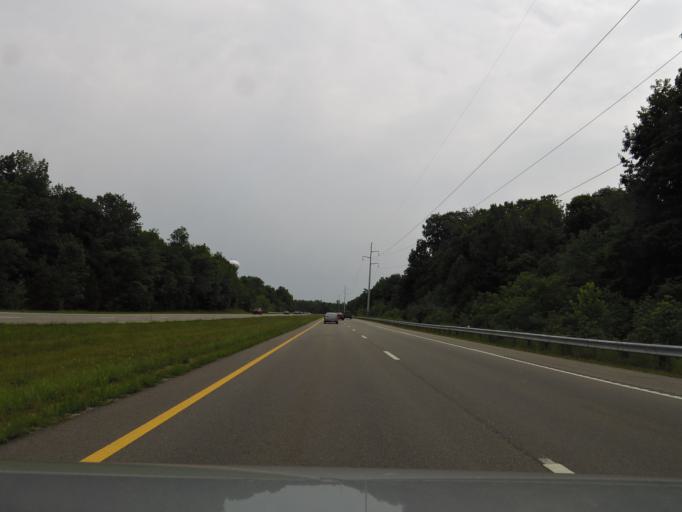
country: US
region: Ohio
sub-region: Warren County
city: Waynesville
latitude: 39.5053
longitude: -84.0223
